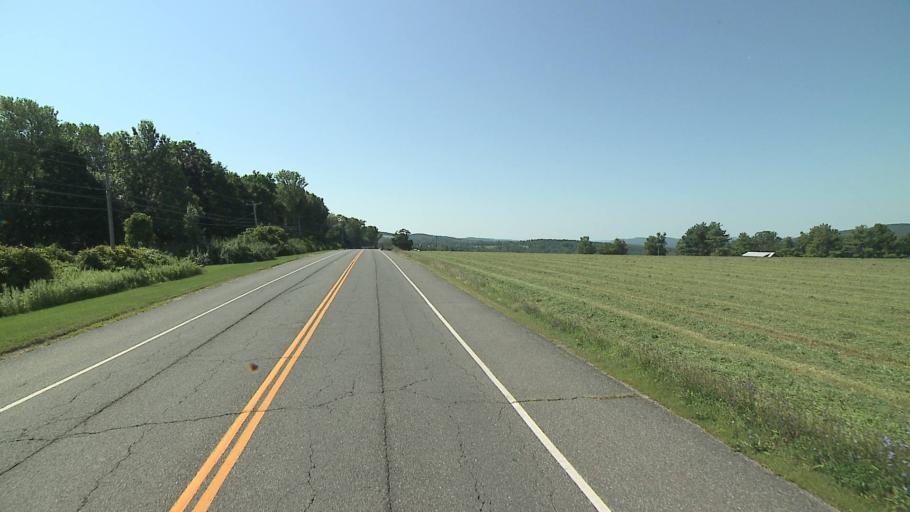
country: US
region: Connecticut
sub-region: Litchfield County
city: Canaan
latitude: 41.9278
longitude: -73.4439
